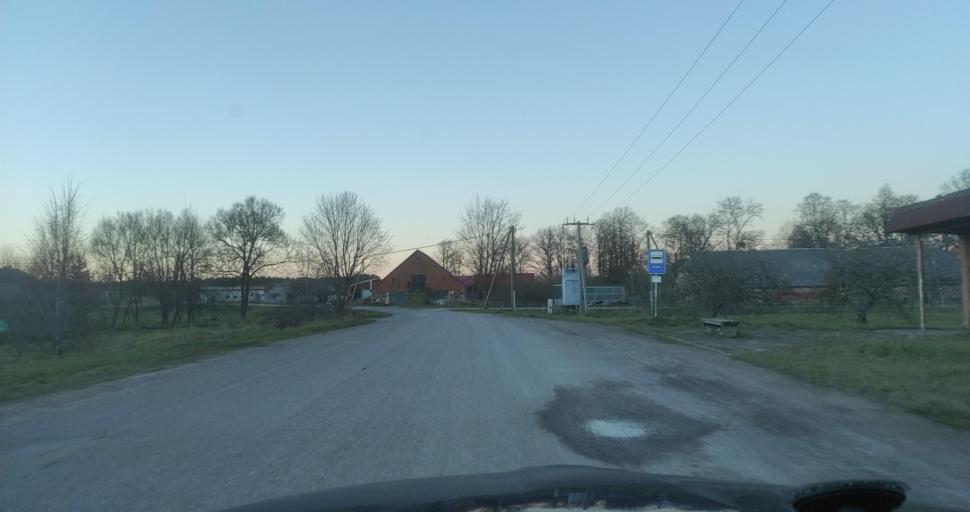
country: LV
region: Dundaga
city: Dundaga
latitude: 57.3747
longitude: 22.2306
